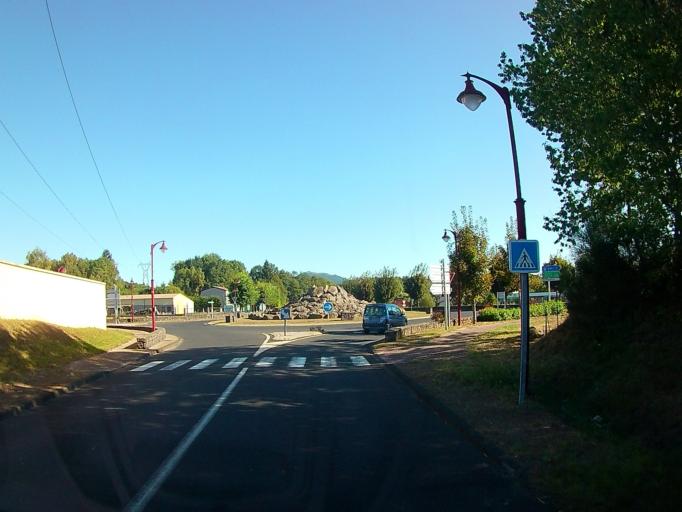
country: FR
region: Auvergne
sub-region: Departement du Puy-de-Dome
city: Saint-Ours
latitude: 45.8515
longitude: 2.8961
